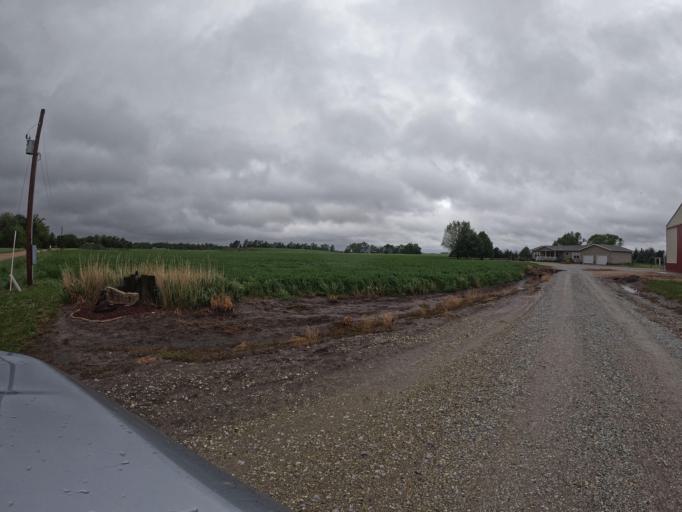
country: US
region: Nebraska
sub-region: Clay County
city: Harvard
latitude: 40.6290
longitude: -98.0993
